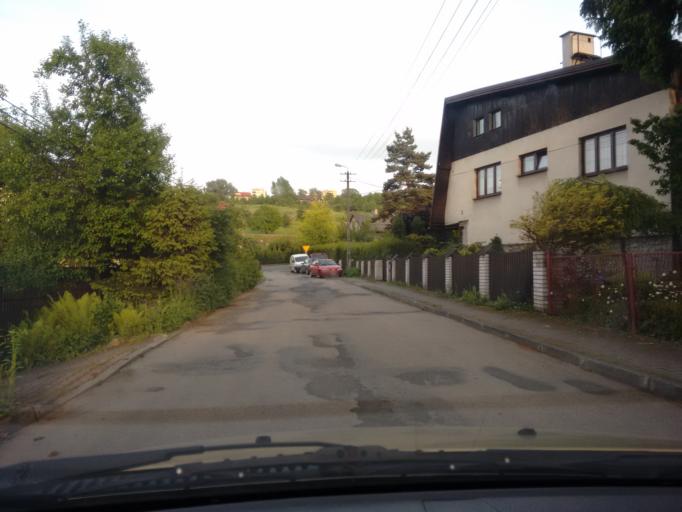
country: PL
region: Silesian Voivodeship
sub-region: Powiat cieszynski
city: Cieszyn
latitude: 49.7473
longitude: 18.6457
